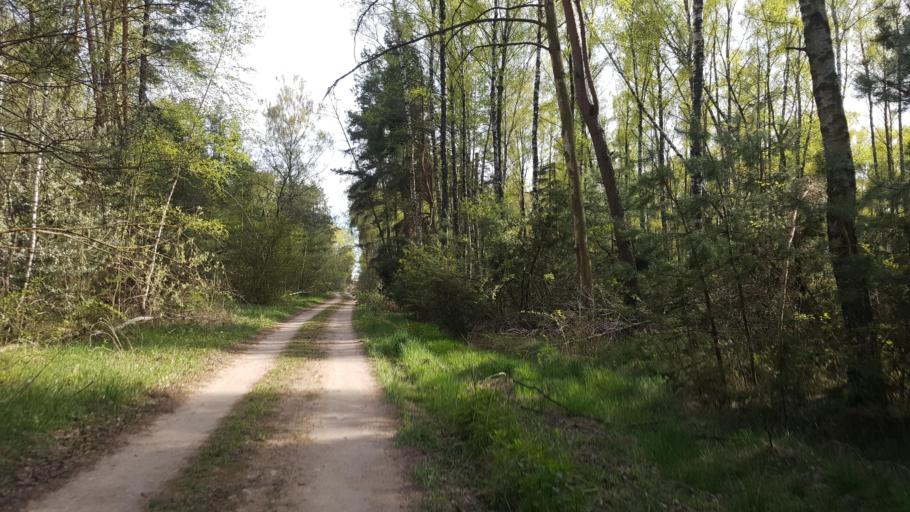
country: BY
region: Brest
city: Vysokaye
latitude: 52.4050
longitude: 23.4723
